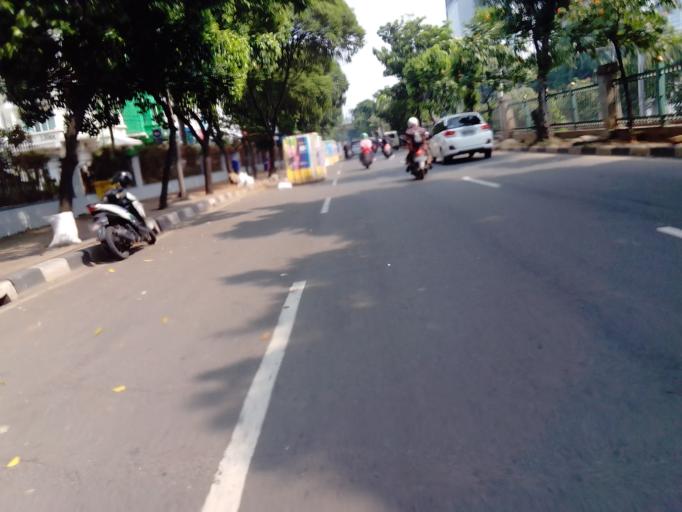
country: ID
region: Jakarta Raya
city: Jakarta
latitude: -6.2212
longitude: 106.7912
